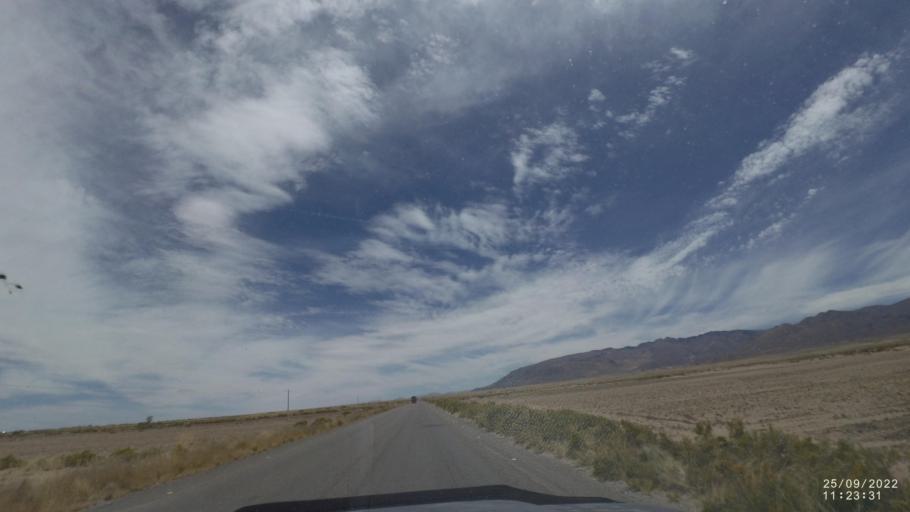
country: BO
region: Oruro
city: Challapata
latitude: -19.1079
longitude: -66.7711
